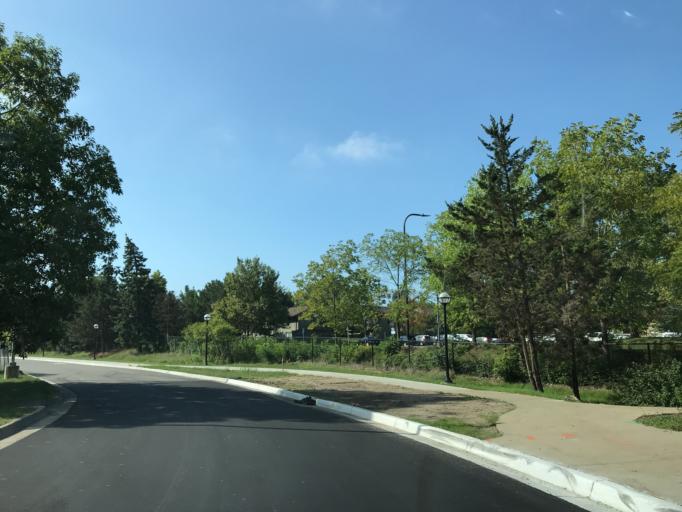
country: US
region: Michigan
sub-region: Washtenaw County
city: Ann Arbor
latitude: 42.3006
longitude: -83.7087
